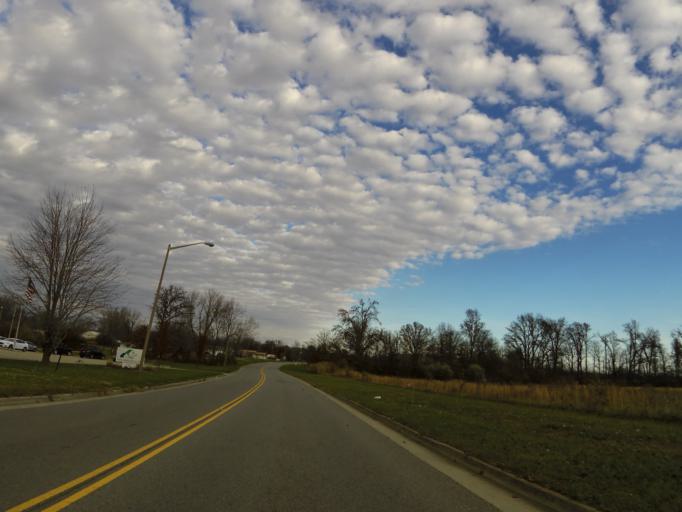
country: US
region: Illinois
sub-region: Jefferson County
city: Mount Vernon
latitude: 38.3125
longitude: -88.9692
